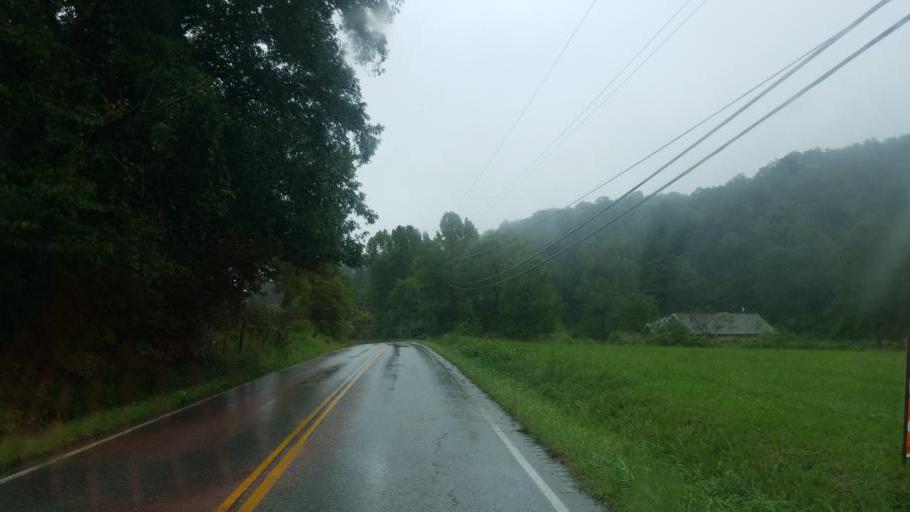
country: US
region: Kentucky
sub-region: Greenup County
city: South Shore
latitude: 38.7087
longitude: -82.9496
